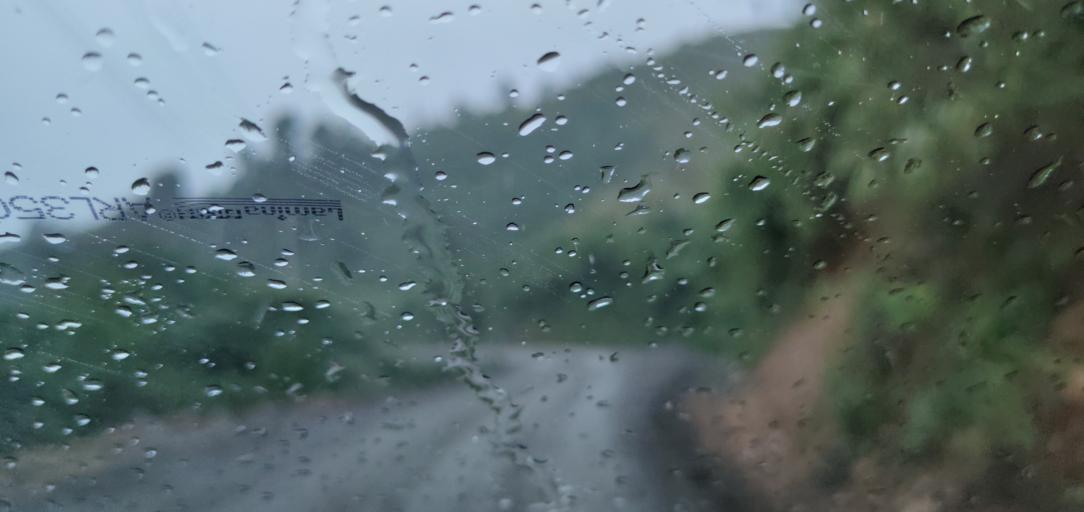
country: LA
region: Phongsali
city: Phongsali
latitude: 21.4297
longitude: 102.1620
